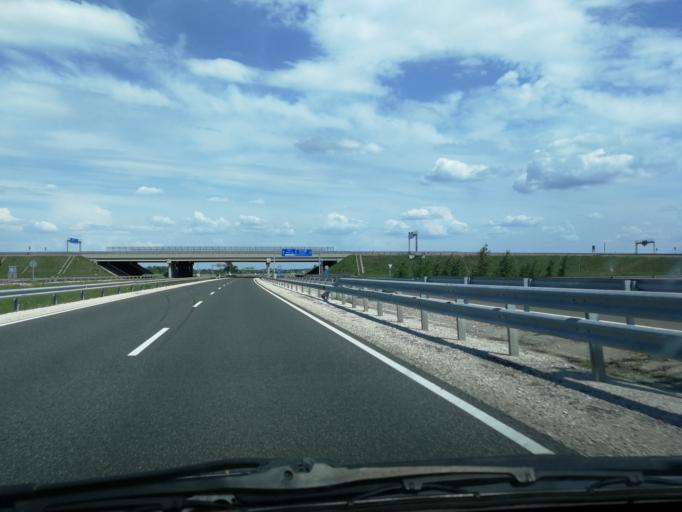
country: HU
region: Tolna
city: Szekszard
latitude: 46.3810
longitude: 18.7512
